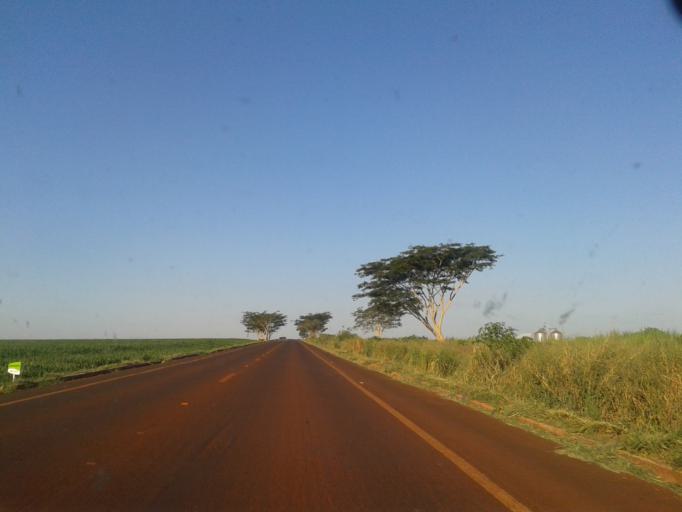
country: BR
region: Minas Gerais
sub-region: Capinopolis
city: Capinopolis
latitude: -18.6996
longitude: -49.6494
